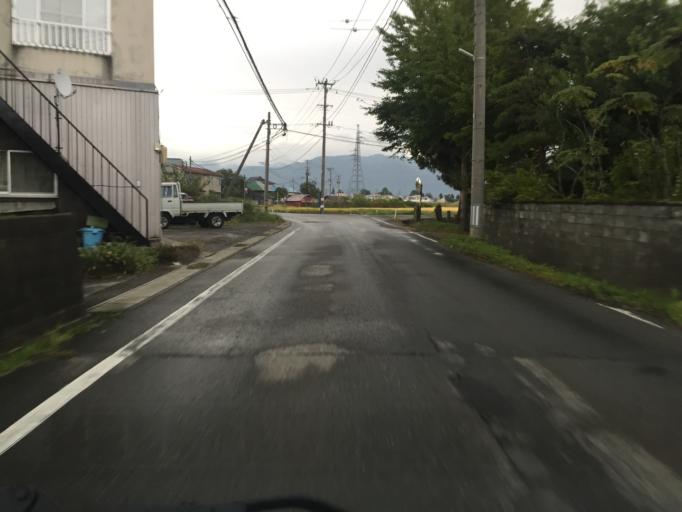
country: JP
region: Fukushima
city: Kitakata
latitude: 37.4979
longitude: 139.8984
